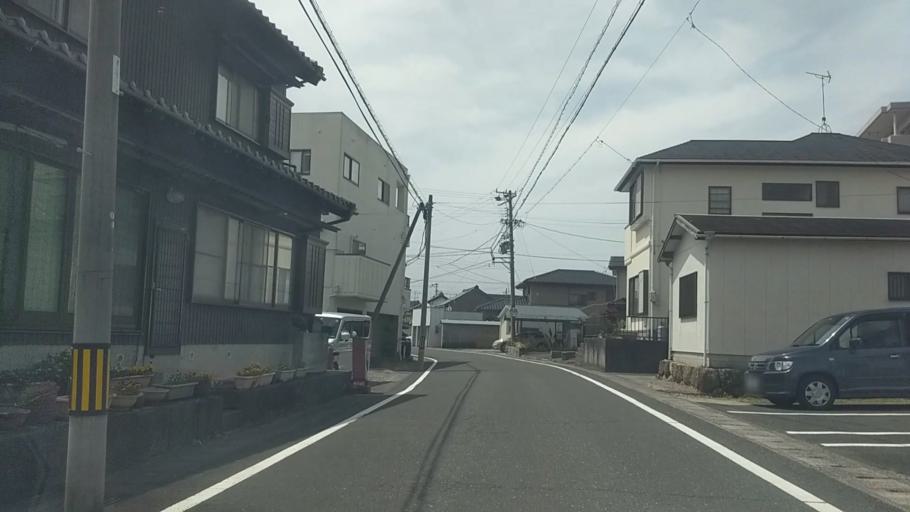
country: JP
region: Shizuoka
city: Kosai-shi
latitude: 34.7517
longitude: 137.5292
